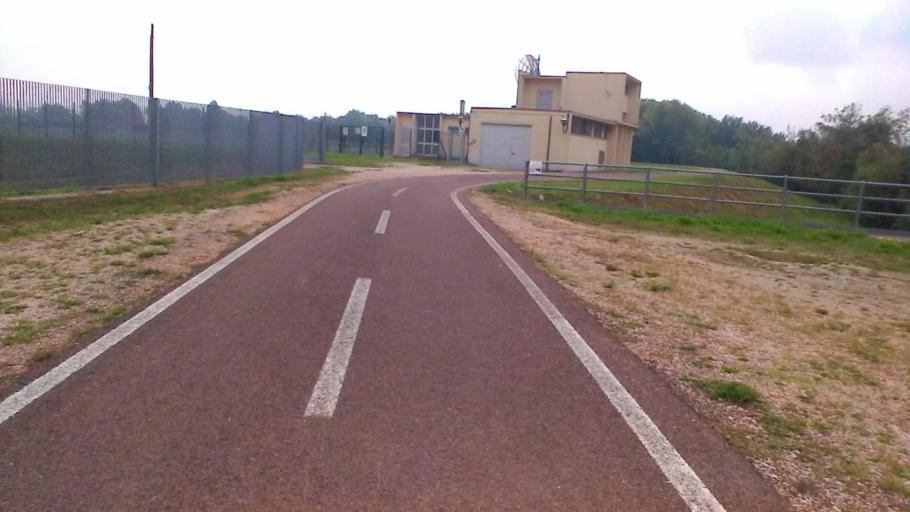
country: IT
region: Veneto
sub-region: Provincia di Verona
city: San Giovanni Lupatoto
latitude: 45.3871
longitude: 11.0641
